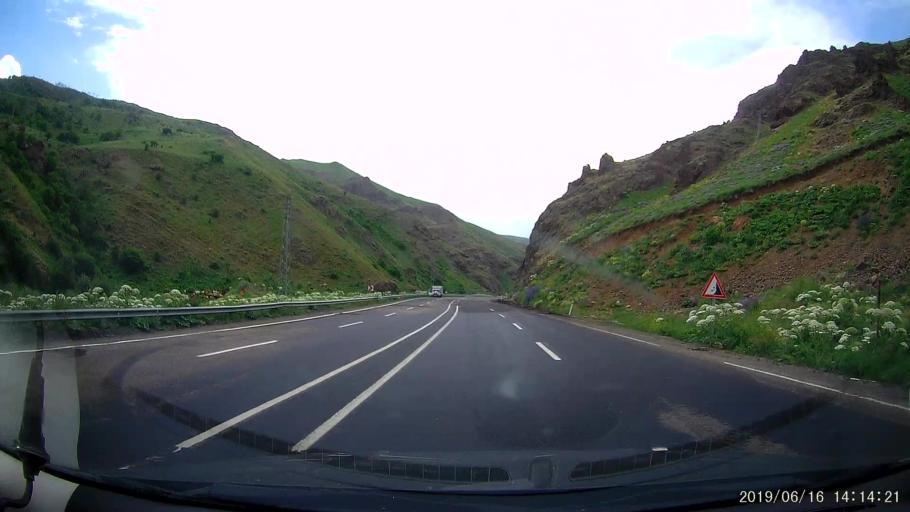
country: TR
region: Agri
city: Tahir
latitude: 39.7955
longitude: 42.4991
